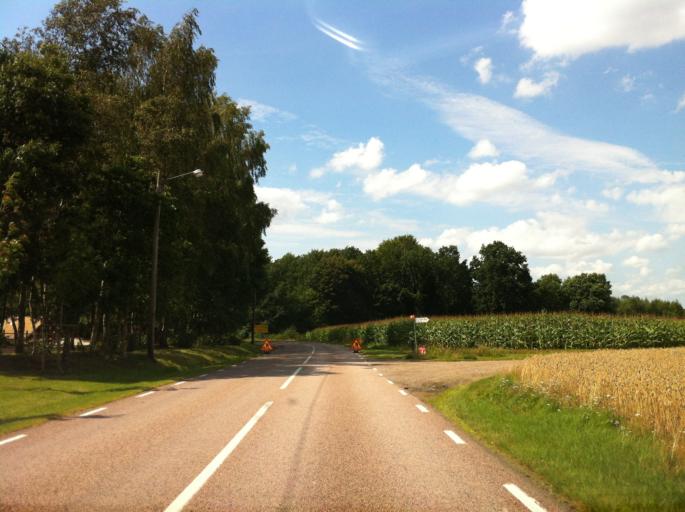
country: SE
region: Skane
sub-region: Klippans Kommun
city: Ljungbyhed
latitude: 56.0608
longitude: 13.2318
